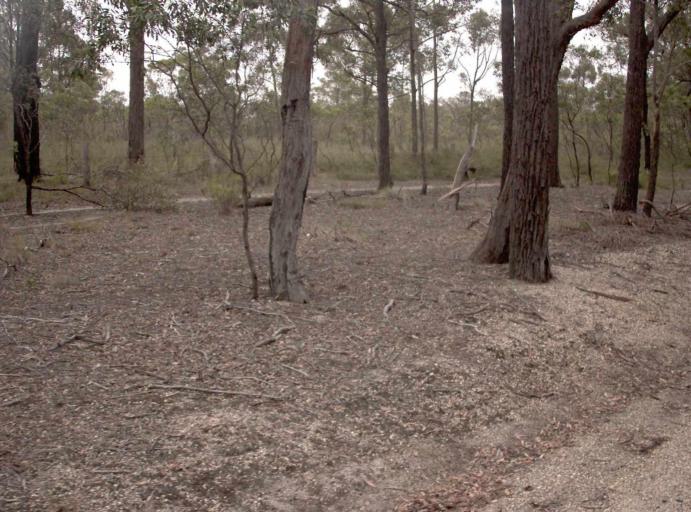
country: AU
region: Victoria
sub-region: Wellington
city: Heyfield
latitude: -37.9478
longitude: 146.7666
